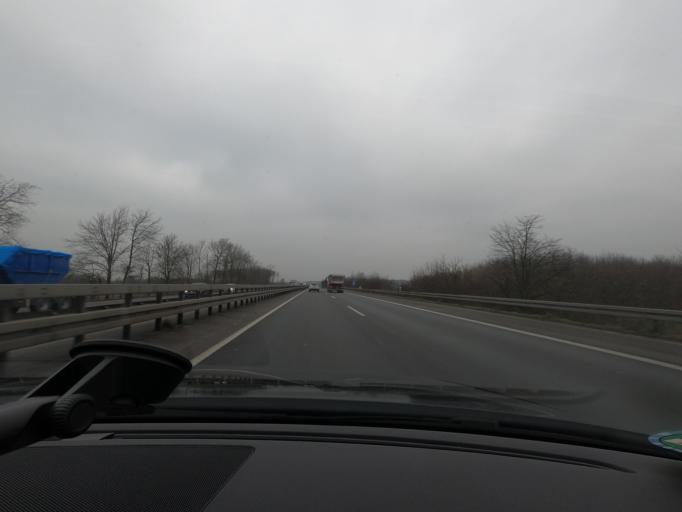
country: DE
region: North Rhine-Westphalia
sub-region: Regierungsbezirk Dusseldorf
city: Viersen
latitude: 51.2505
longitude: 6.3610
